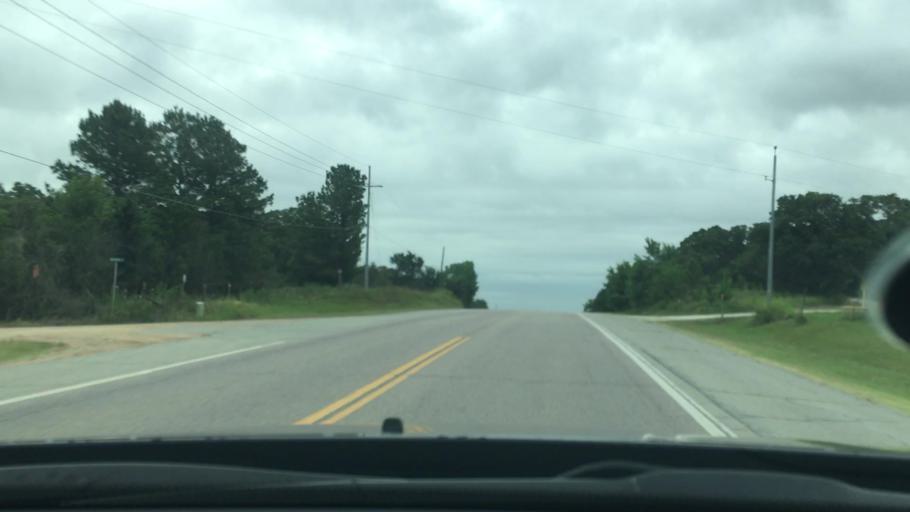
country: US
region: Oklahoma
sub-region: Coal County
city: Coalgate
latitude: 34.5563
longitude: -96.2411
